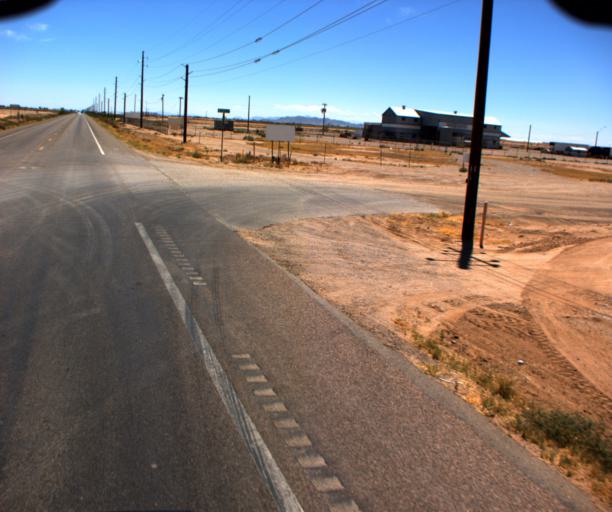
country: US
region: Arizona
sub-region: Pinal County
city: Casa Grande
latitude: 32.8794
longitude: -111.9124
